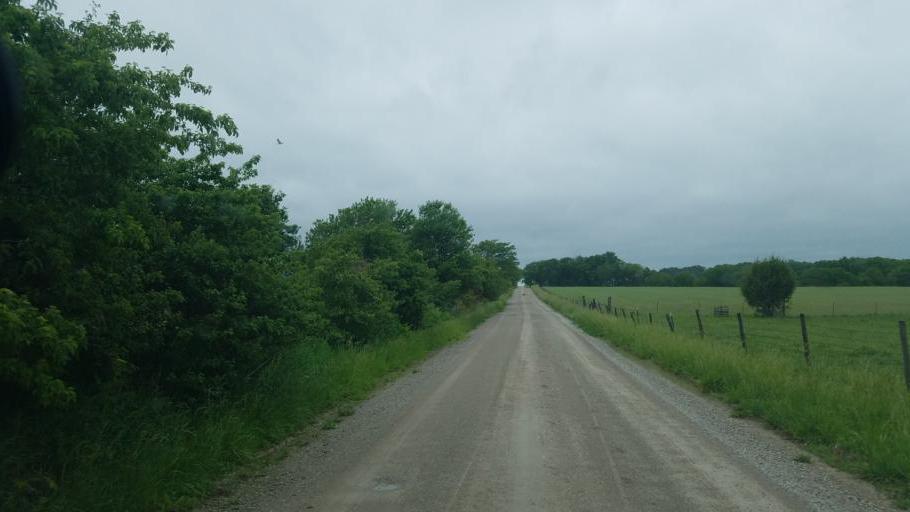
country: US
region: Missouri
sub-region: Carroll County
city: Carrollton
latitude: 39.4851
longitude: -93.4843
